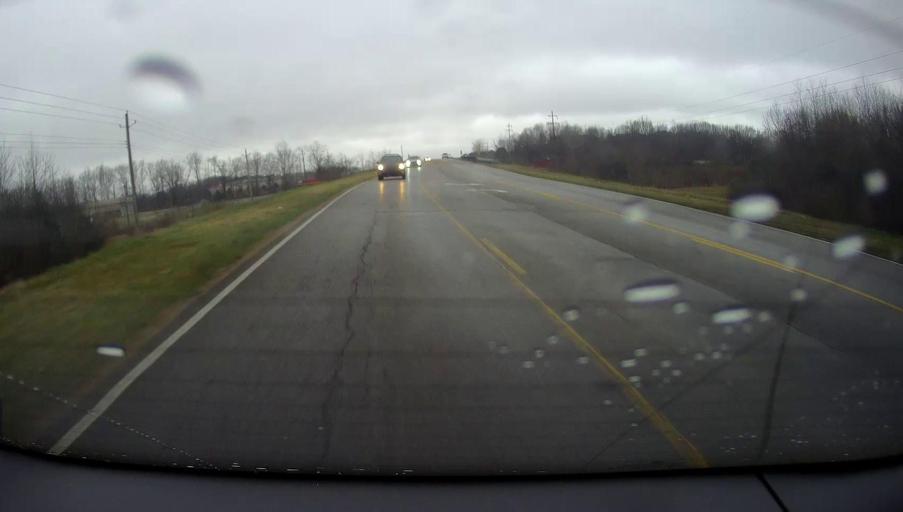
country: US
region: Mississippi
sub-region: Alcorn County
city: Corinth
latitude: 34.9090
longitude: -88.5110
